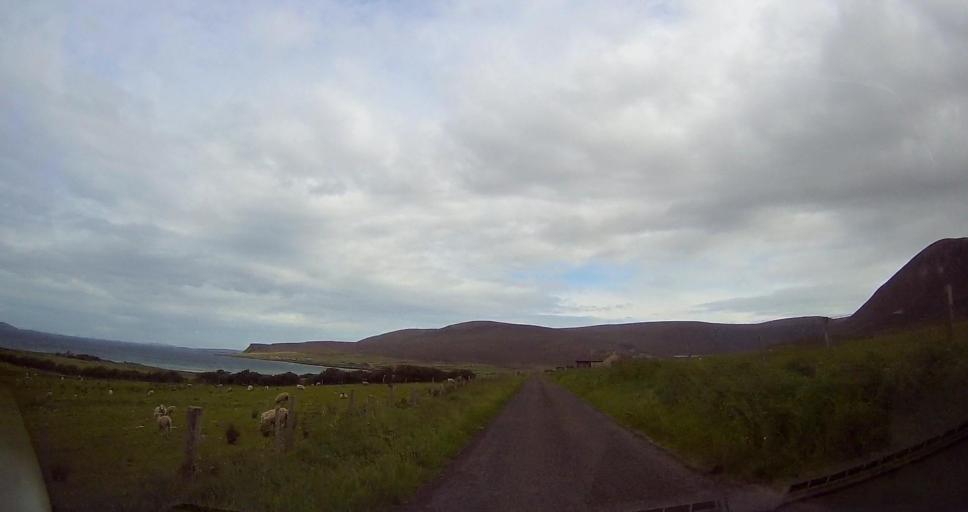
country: GB
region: Scotland
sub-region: Orkney Islands
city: Stromness
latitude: 58.9139
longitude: -3.3239
